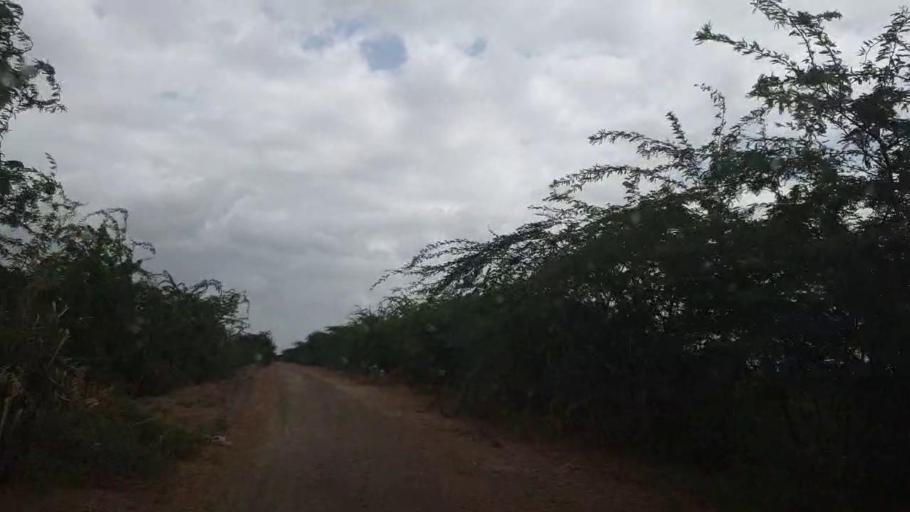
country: PK
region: Sindh
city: Badin
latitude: 24.6458
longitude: 68.9456
